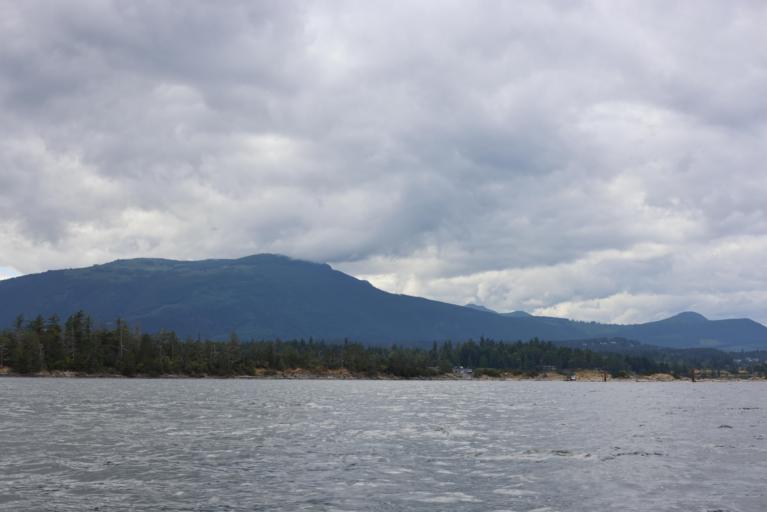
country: CA
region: British Columbia
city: North Cowichan
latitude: 48.9135
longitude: -123.6771
